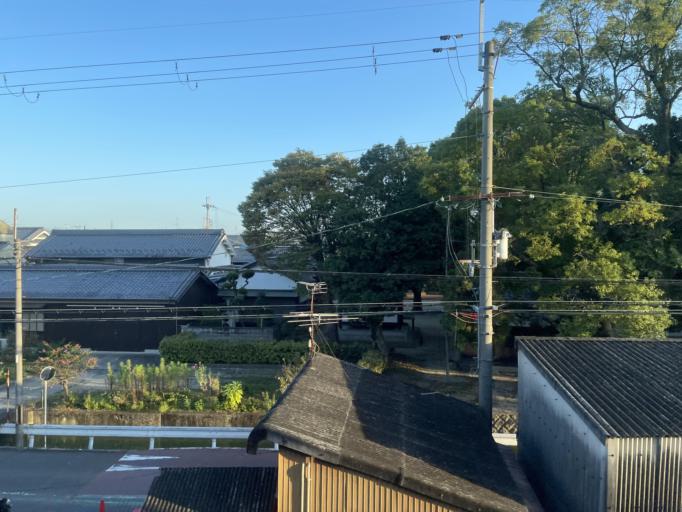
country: JP
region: Nara
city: Kashihara-shi
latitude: 34.5204
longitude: 135.7600
